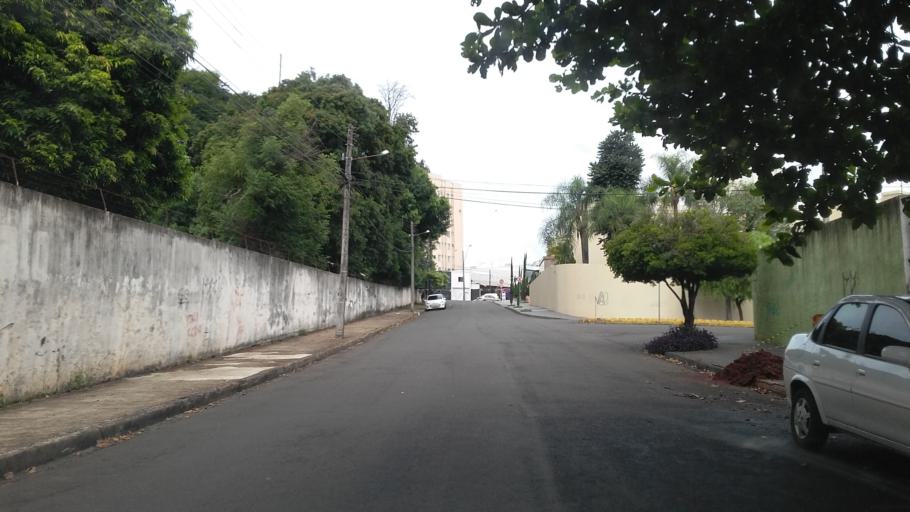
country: BR
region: Parana
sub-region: Londrina
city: Londrina
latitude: -23.3044
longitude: -51.1742
